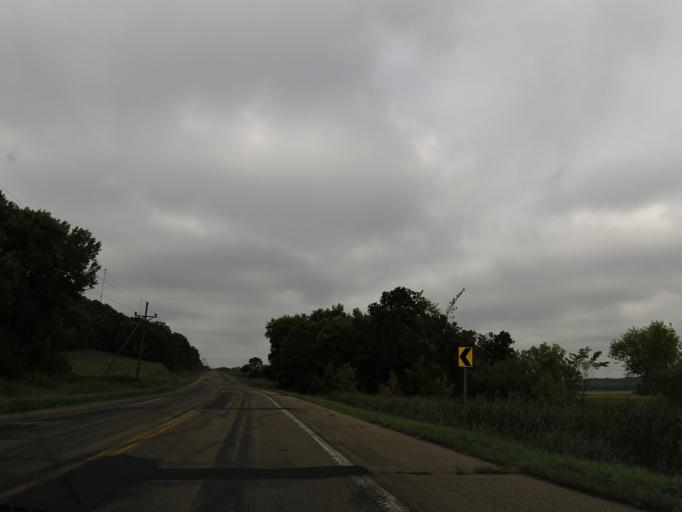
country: US
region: Minnesota
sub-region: Yellow Medicine County
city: Granite Falls
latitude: 44.8523
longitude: -95.6210
